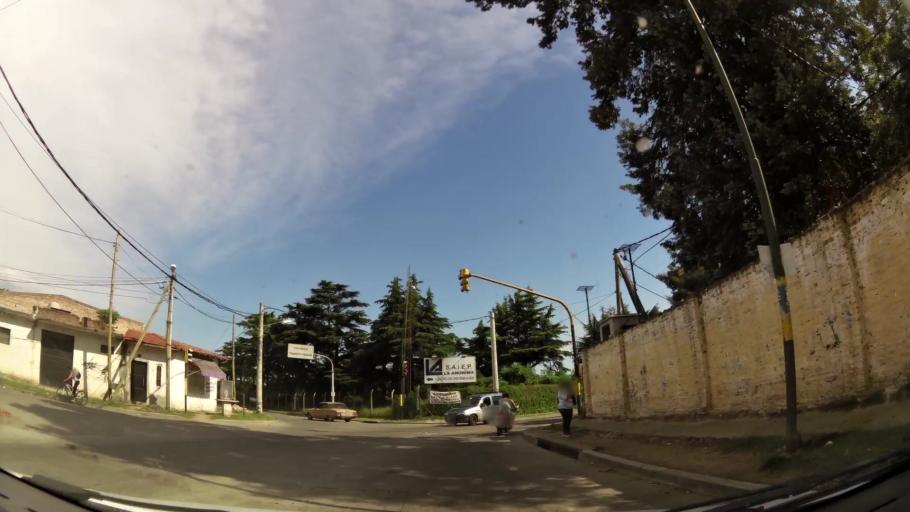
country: AR
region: Buenos Aires
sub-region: Partido de Merlo
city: Merlo
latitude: -34.6342
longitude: -58.7113
